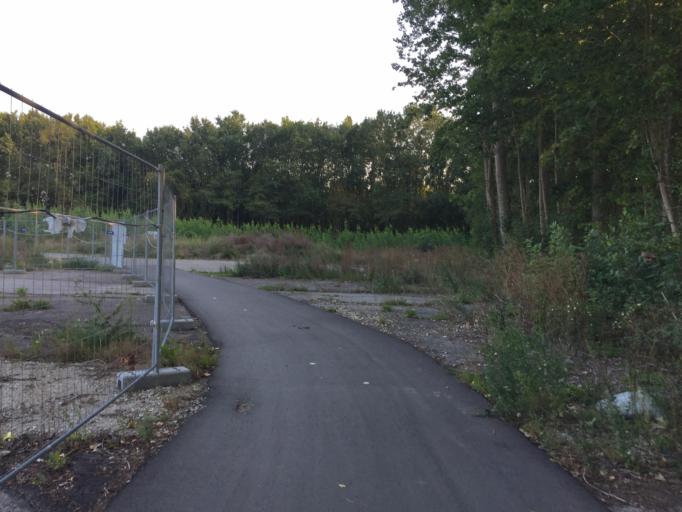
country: DK
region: South Denmark
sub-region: Odense Kommune
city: Odense
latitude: 55.3716
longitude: 10.4039
